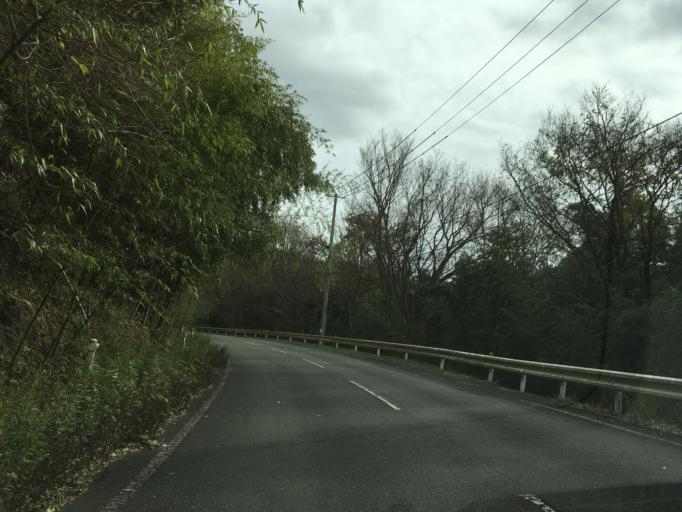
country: JP
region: Iwate
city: Ichinoseki
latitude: 38.7894
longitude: 141.2615
